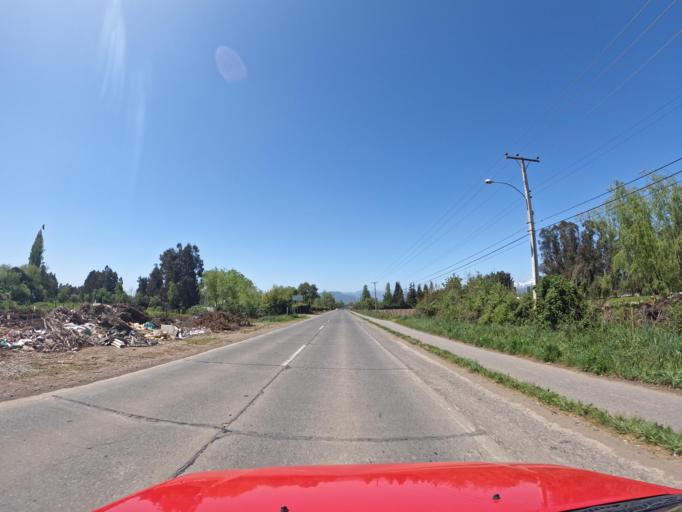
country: CL
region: Maule
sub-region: Provincia de Linares
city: Linares
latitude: -35.8296
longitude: -71.5076
